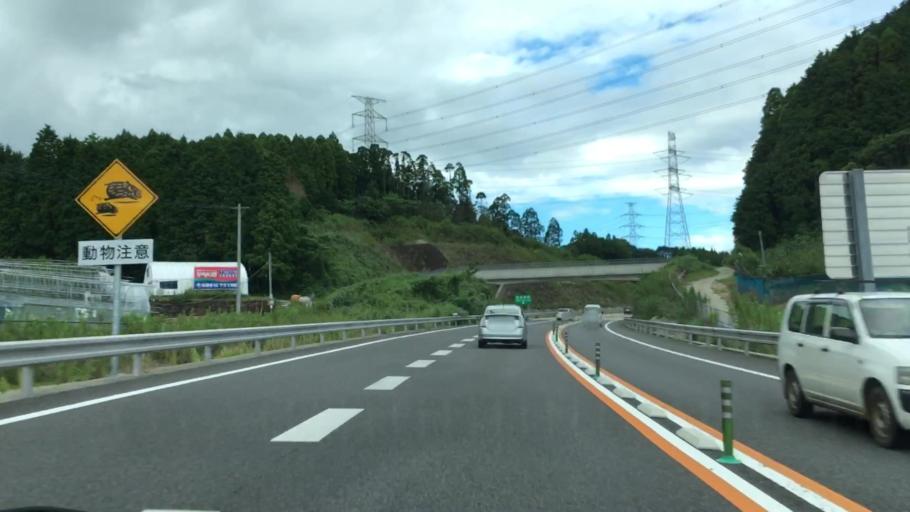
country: JP
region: Saga Prefecture
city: Imaricho-ko
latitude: 33.3503
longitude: 129.9244
